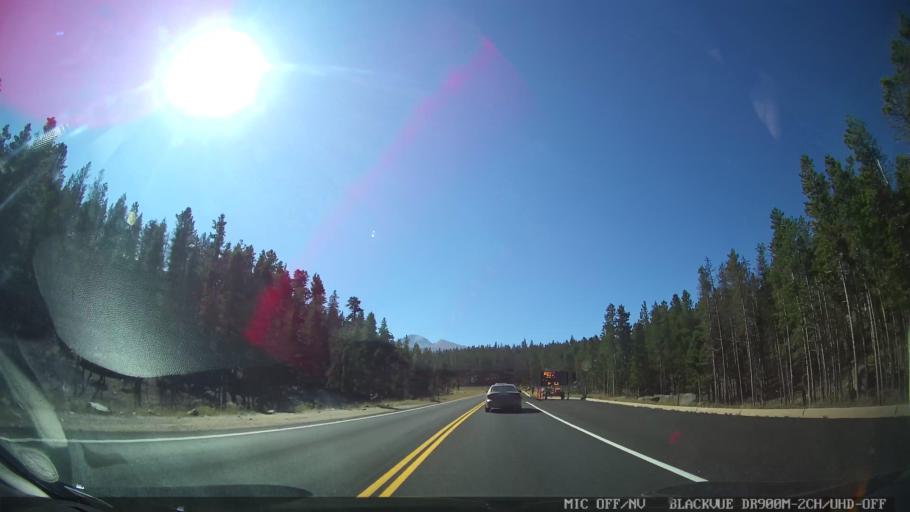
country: US
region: Colorado
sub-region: Larimer County
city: Estes Park
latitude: 40.3378
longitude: -105.6007
